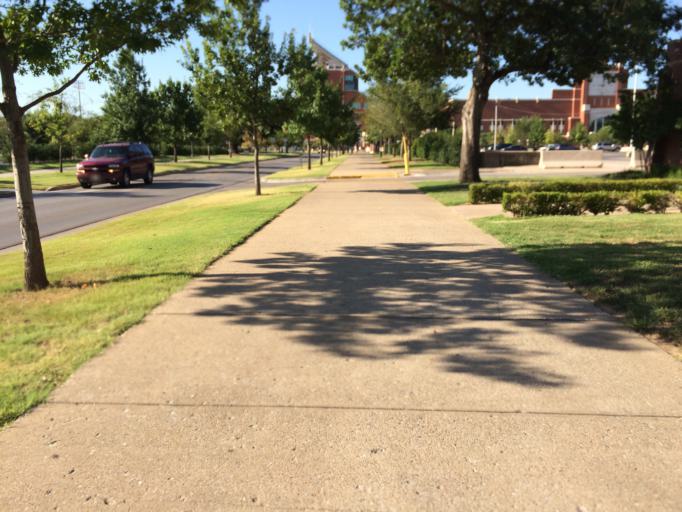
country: US
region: Oklahoma
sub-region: Cleveland County
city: Norman
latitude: 35.2089
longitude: -97.4414
